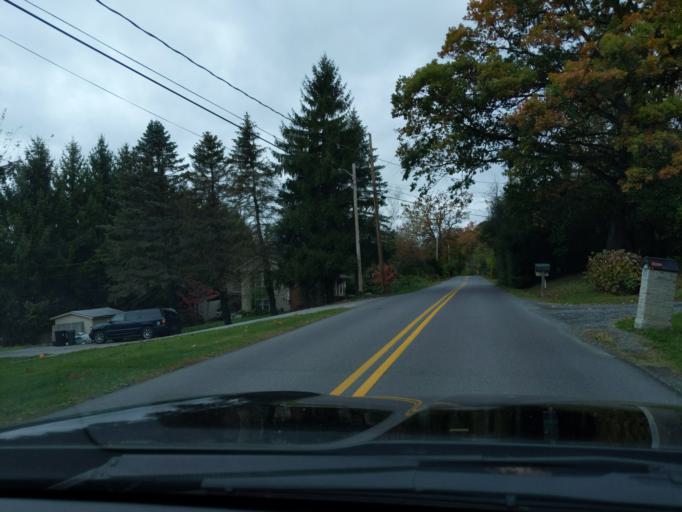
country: US
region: Pennsylvania
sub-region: Blair County
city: Lakemont
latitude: 40.4550
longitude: -78.3909
